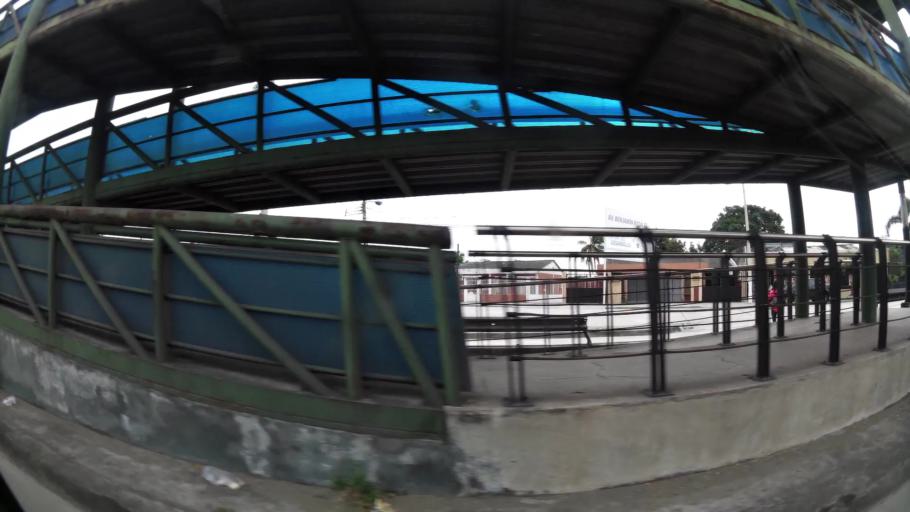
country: EC
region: Guayas
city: Eloy Alfaro
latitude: -2.1490
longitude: -79.8766
